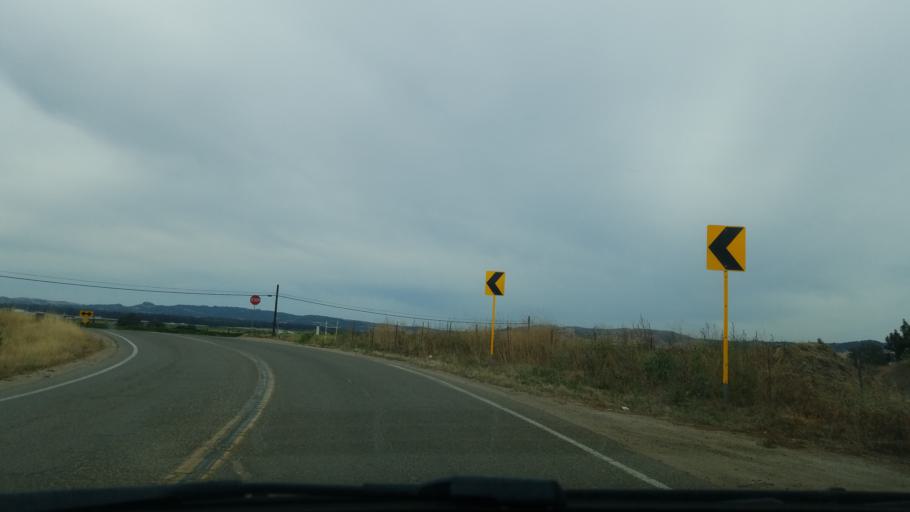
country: US
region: California
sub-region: Santa Barbara County
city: Orcutt
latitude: 34.9093
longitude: -120.4902
